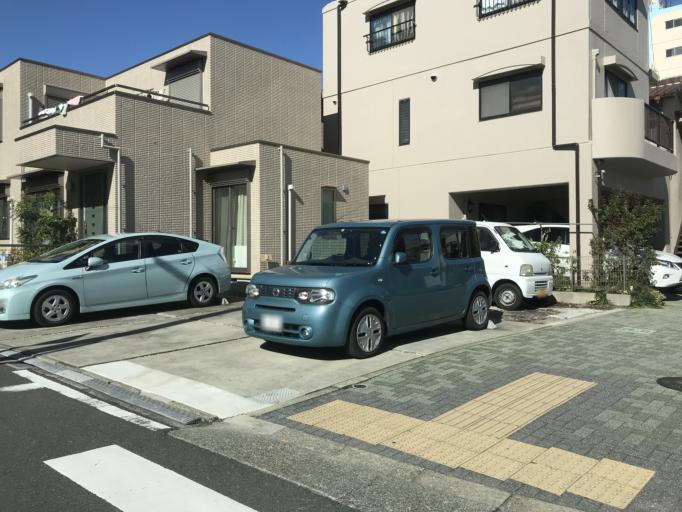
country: JP
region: Aichi
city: Nagoya-shi
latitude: 35.1786
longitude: 136.9397
